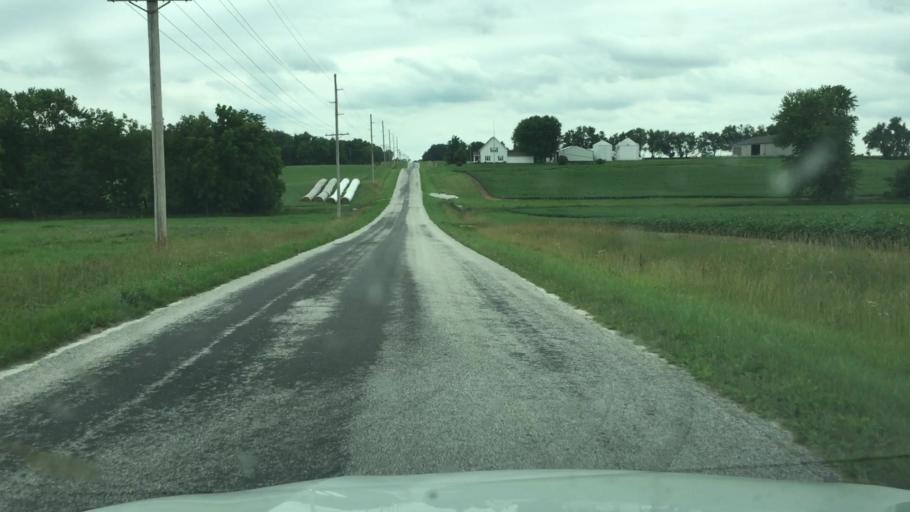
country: US
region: Illinois
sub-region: Hancock County
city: Carthage
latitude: 40.3011
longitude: -91.0831
